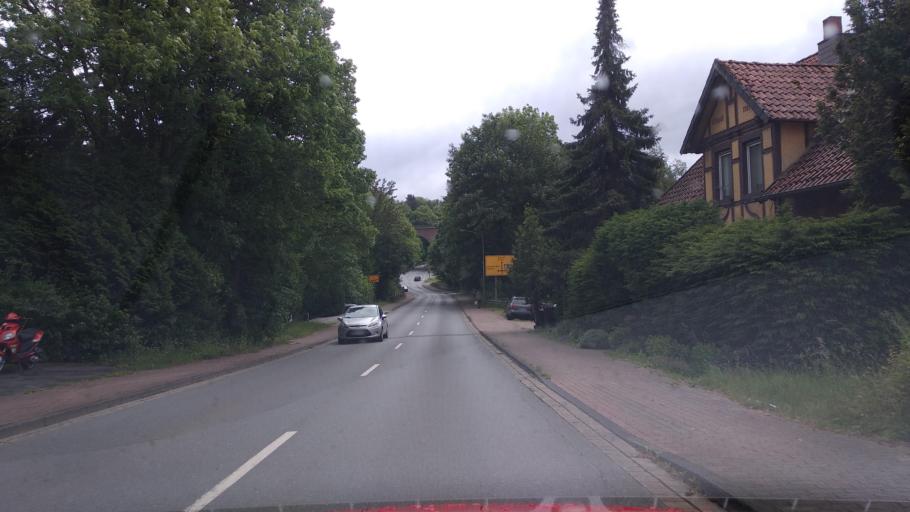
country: DE
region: Lower Saxony
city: Buchholz
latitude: 52.2227
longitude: 9.1191
